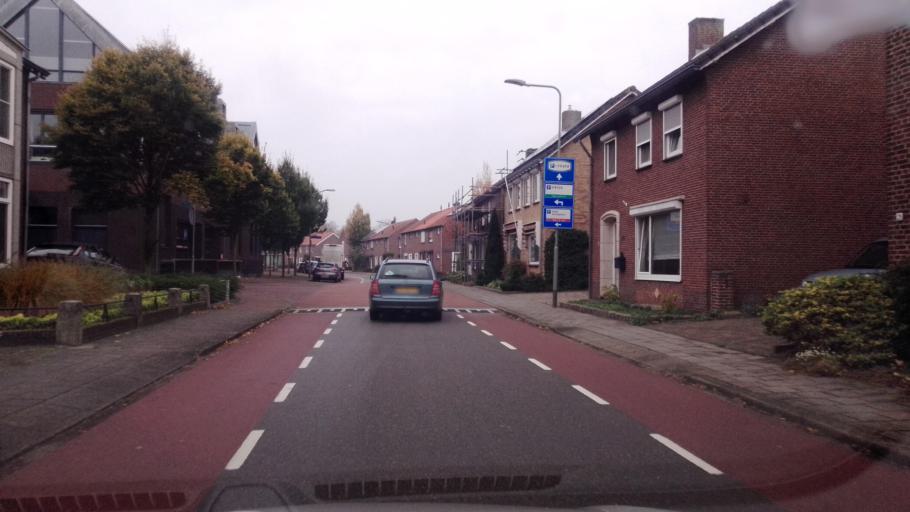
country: NL
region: Limburg
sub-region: Gemeente Peel en Maas
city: Maasbree
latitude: 51.4548
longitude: 6.0545
